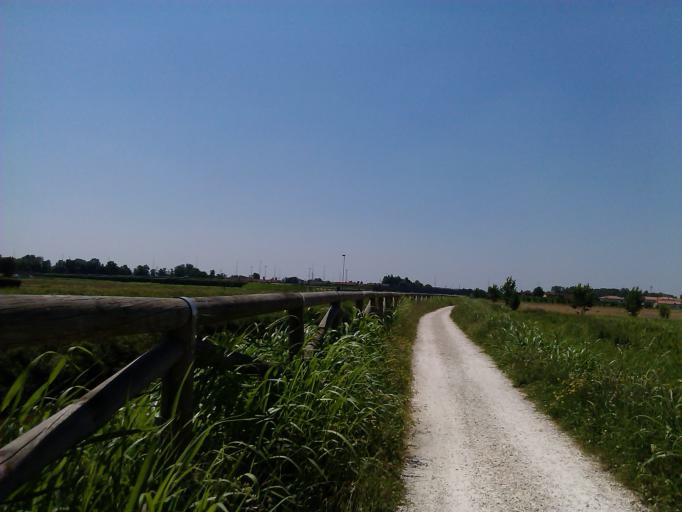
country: IT
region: Veneto
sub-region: Provincia di Treviso
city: Castelfranco Veneto
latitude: 45.6541
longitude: 11.9226
